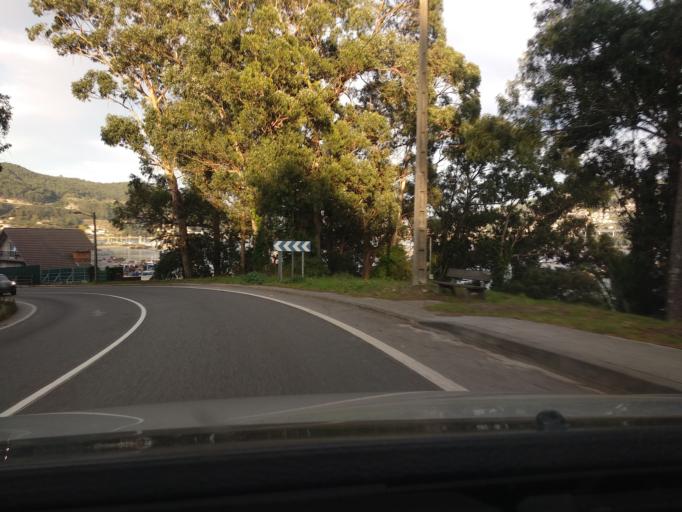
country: ES
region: Galicia
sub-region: Provincia de Pontevedra
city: Vigo
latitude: 42.2829
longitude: -8.6854
